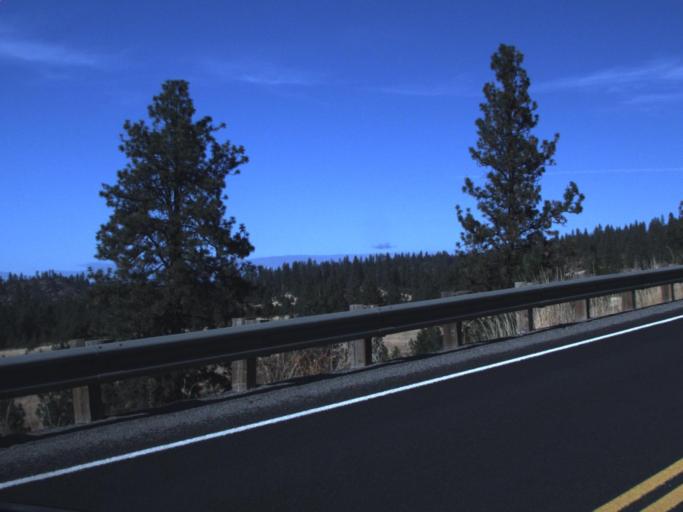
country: US
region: Washington
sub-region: Lincoln County
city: Davenport
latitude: 47.9331
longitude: -118.3202
